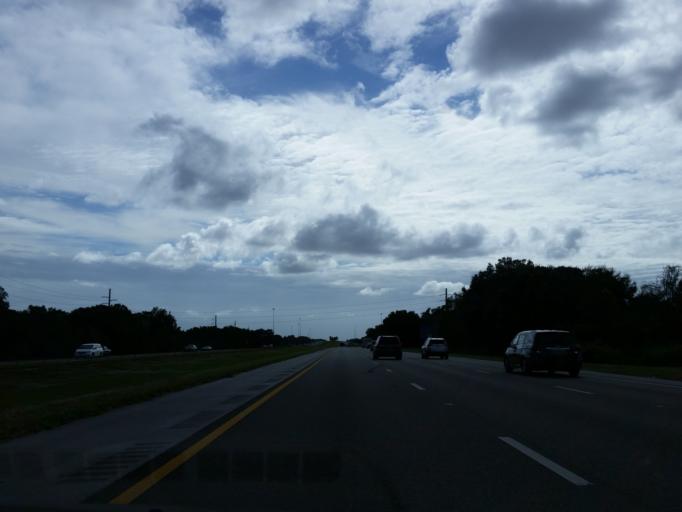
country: US
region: Florida
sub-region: Sarasota County
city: Lake Sarasota
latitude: 27.2808
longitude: -82.4489
